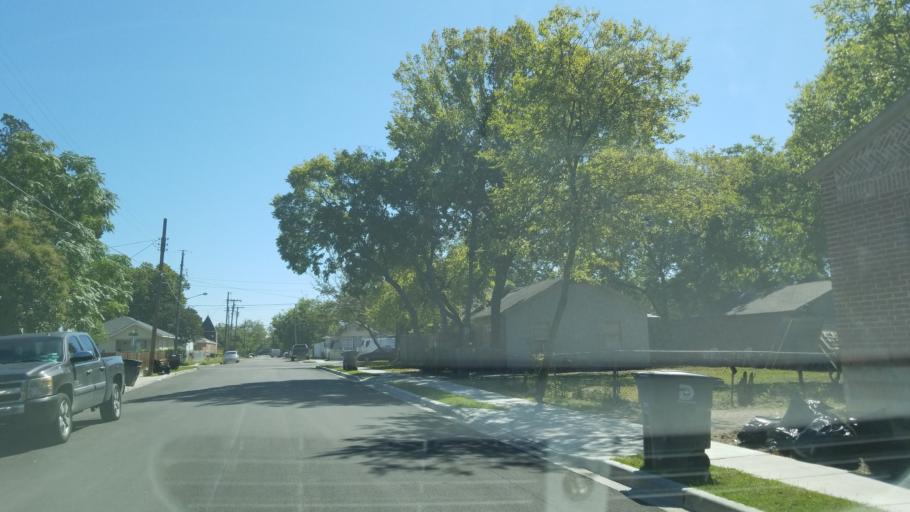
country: US
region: Texas
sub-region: Dallas County
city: Highland Park
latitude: 32.7963
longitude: -96.7571
